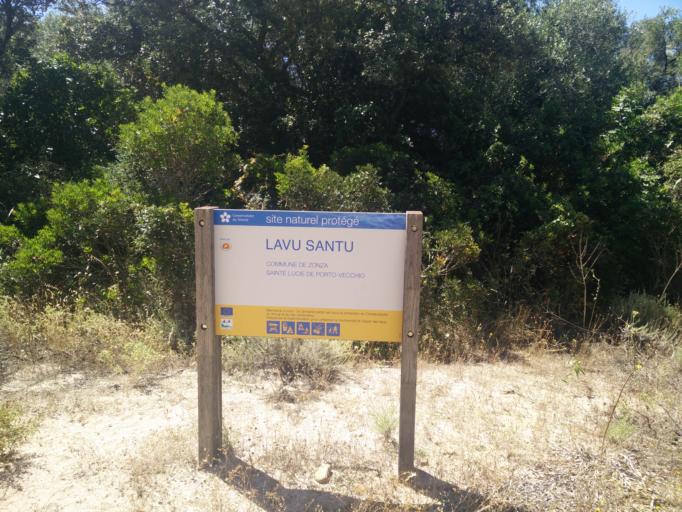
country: FR
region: Corsica
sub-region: Departement de la Corse-du-Sud
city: Sari-Solenzara
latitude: 41.7084
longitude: 9.4000
